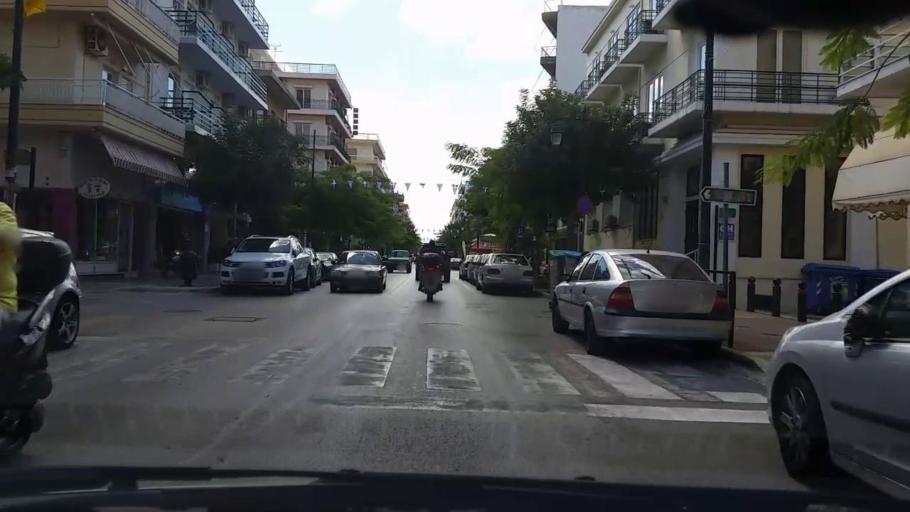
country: GR
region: Peloponnese
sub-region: Nomos Korinthias
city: Loutraki
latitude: 37.9765
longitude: 22.9774
